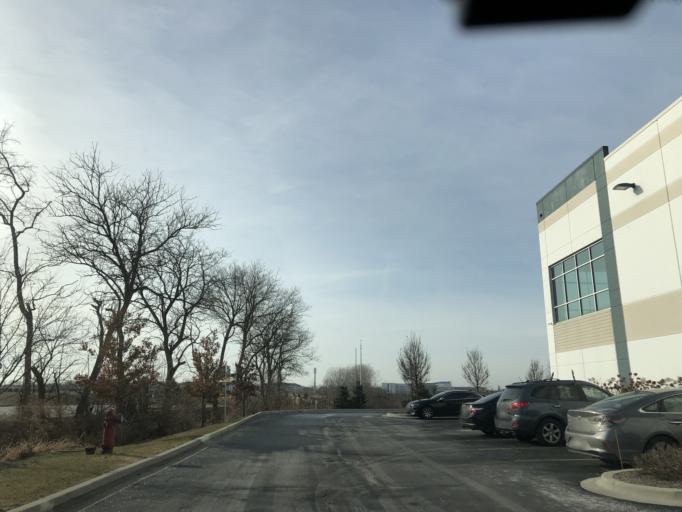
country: US
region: Illinois
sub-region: DuPage County
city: Woodridge
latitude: 41.7145
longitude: -88.0307
